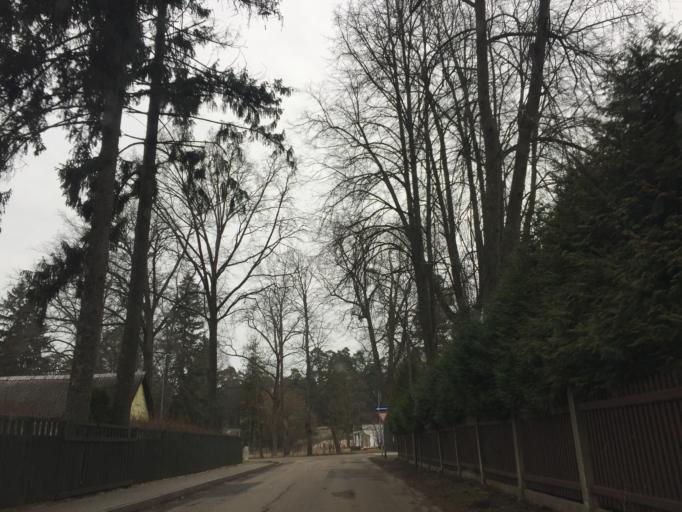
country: LV
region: Jurmala
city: Jurmala
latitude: 56.9639
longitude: 23.7368
